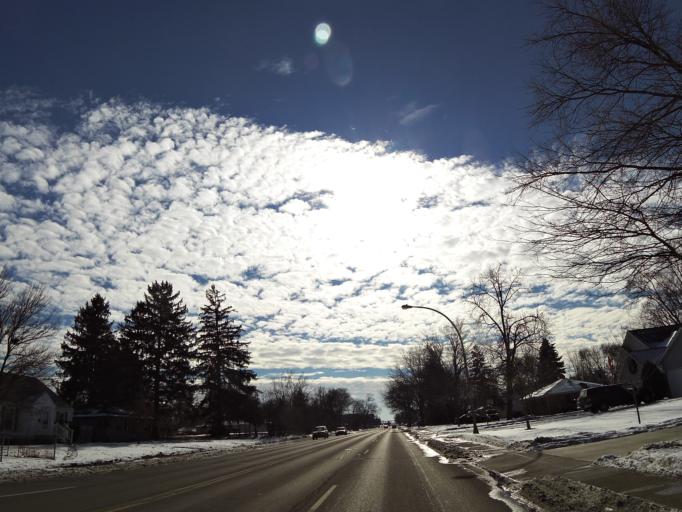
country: US
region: Minnesota
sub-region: Hennepin County
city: Richfield
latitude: 44.8706
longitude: -93.2885
